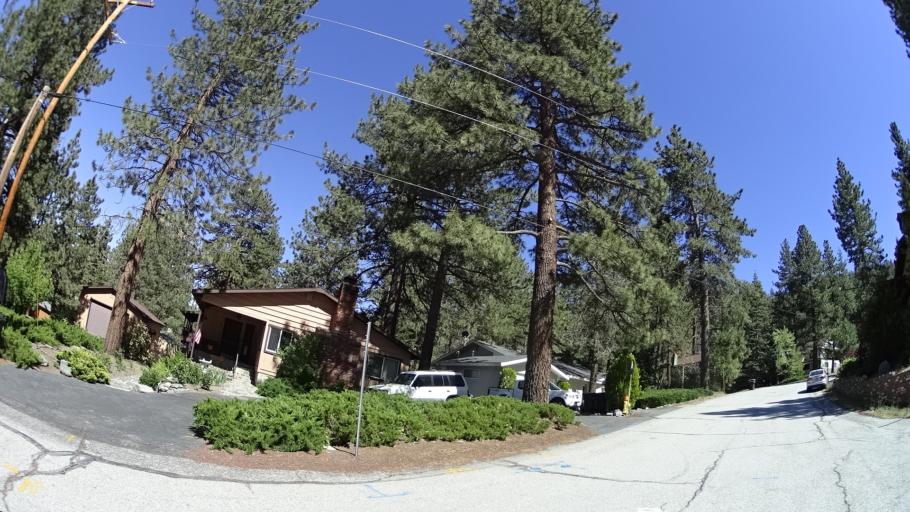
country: US
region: California
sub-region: San Bernardino County
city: Wrightwood
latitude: 34.3618
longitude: -117.6530
